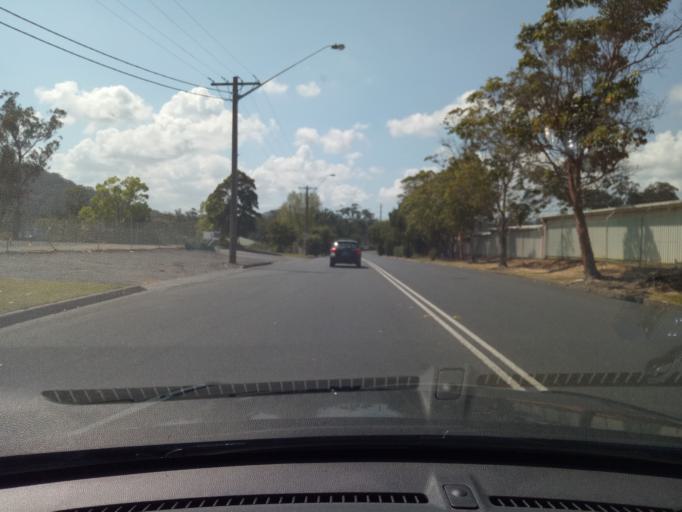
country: AU
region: New South Wales
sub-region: Gosford Shire
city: Gosford
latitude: -33.4207
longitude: 151.3289
